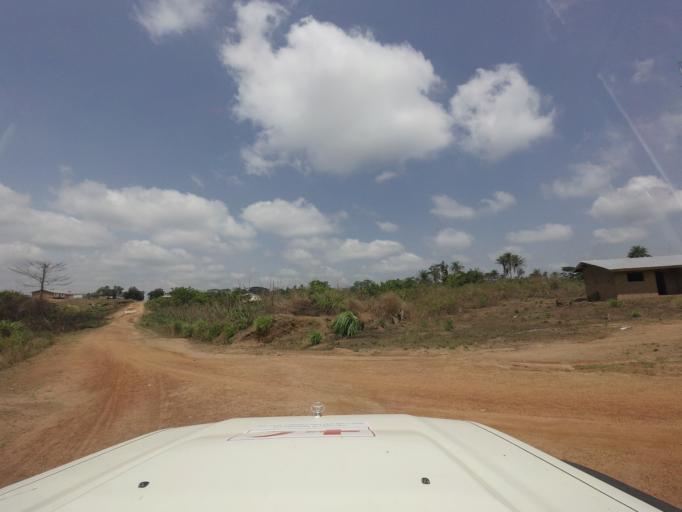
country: LR
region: Lofa
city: Voinjama
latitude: 8.4661
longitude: -9.6650
